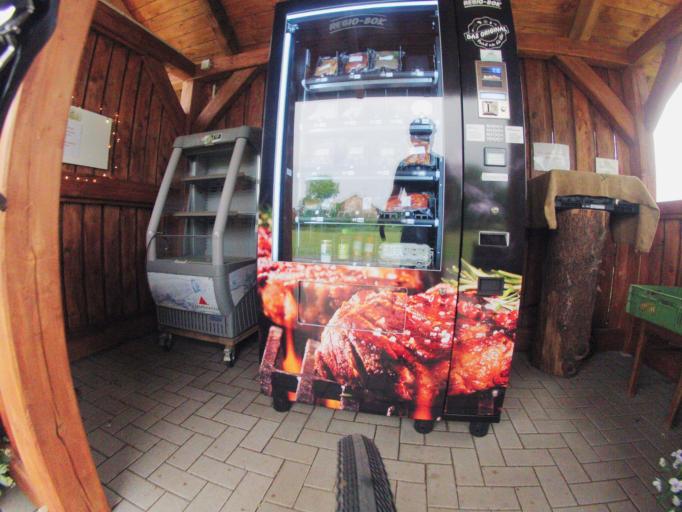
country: DE
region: North Rhine-Westphalia
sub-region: Regierungsbezirk Munster
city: Birgte
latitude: 52.2723
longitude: 7.6746
